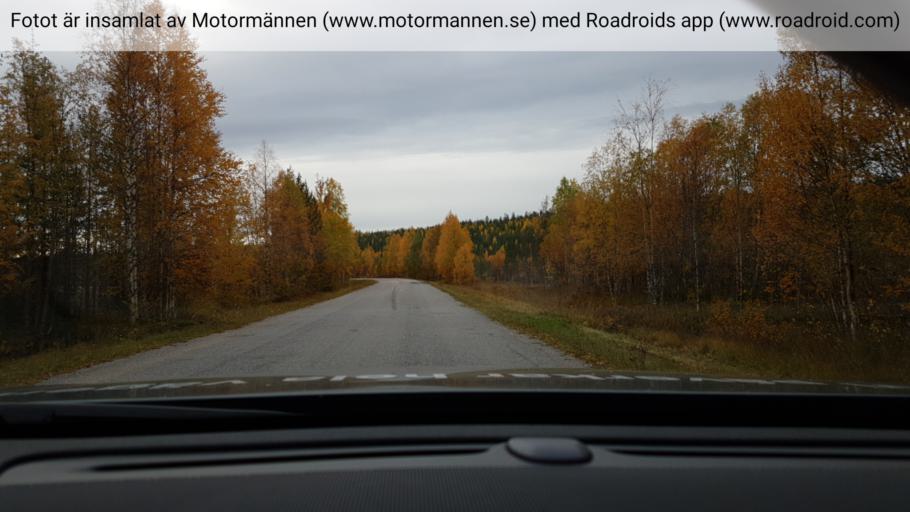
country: SE
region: Norrbotten
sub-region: Overkalix Kommun
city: OEverkalix
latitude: 66.2470
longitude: 23.0057
